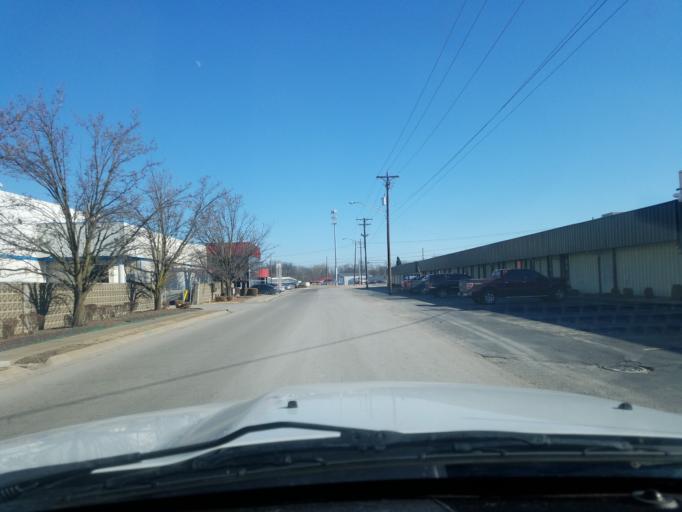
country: US
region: Kentucky
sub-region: Henderson County
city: Henderson
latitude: 37.8045
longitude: -87.6393
